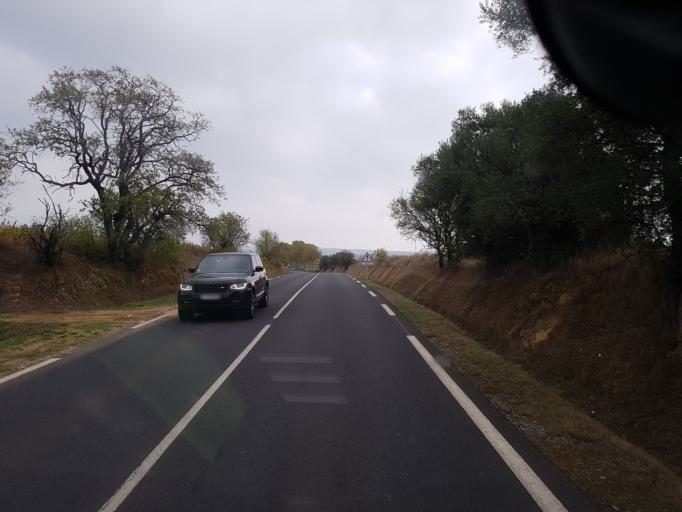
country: FR
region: Languedoc-Roussillon
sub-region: Departement de l'Herault
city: Meze
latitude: 43.4306
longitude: 3.5655
